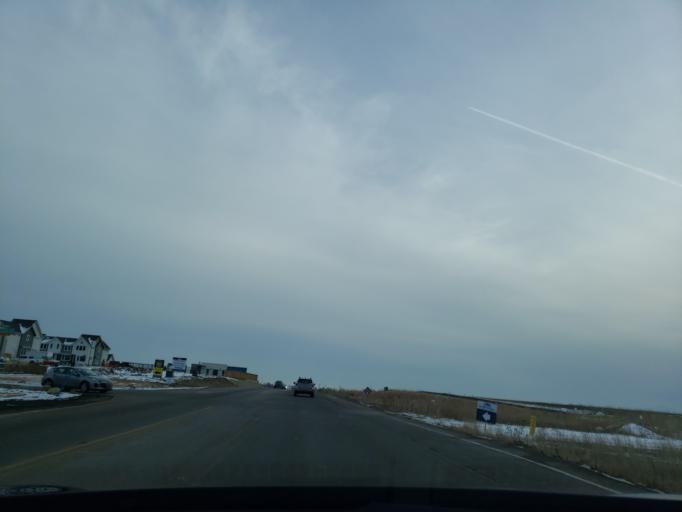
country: US
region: Colorado
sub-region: Larimer County
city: Campion
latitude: 40.3414
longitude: -105.0936
